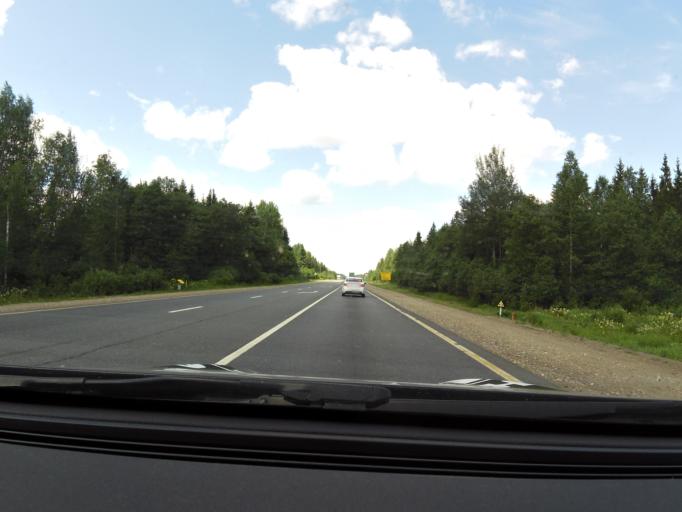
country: RU
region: Tverskaya
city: Kuzhenkino
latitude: 57.7304
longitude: 34.0544
